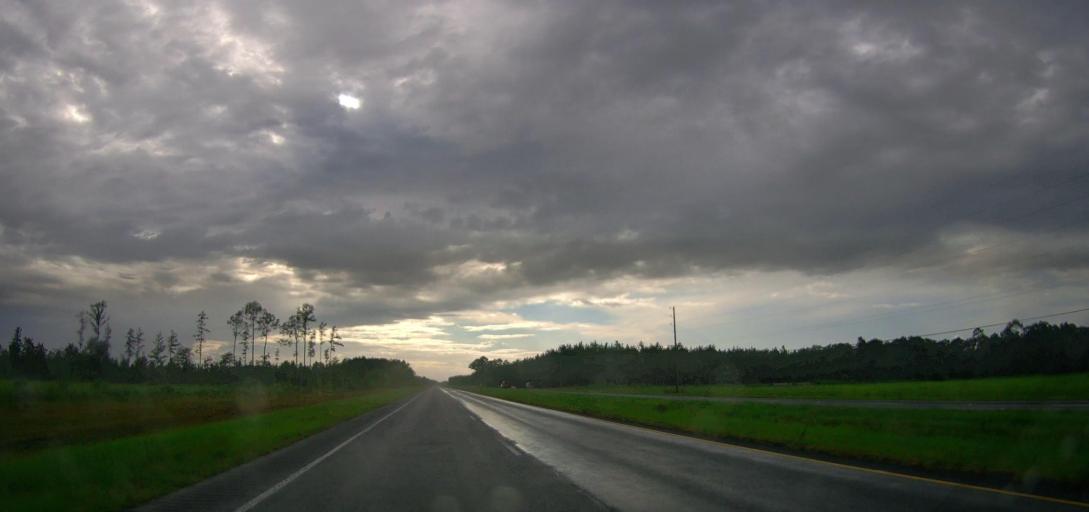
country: US
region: Georgia
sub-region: Ware County
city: Deenwood
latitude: 31.2561
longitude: -82.4898
